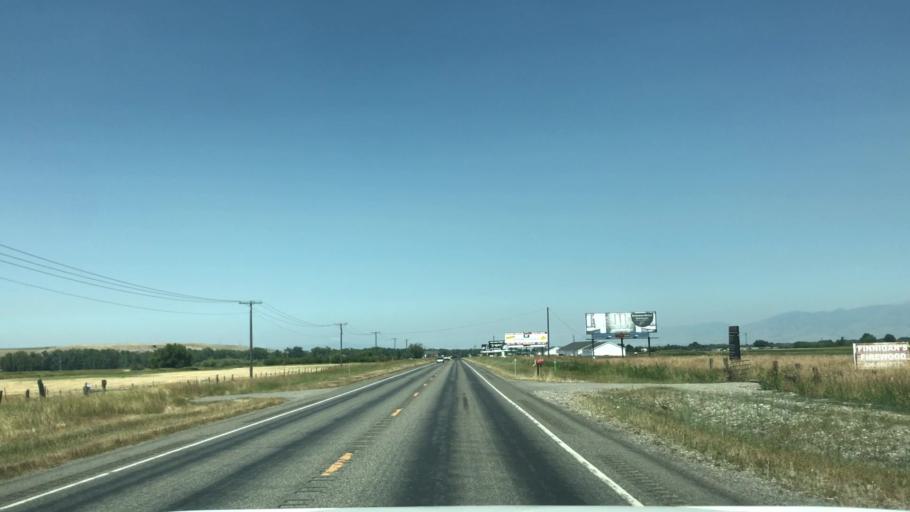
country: US
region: Montana
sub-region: Gallatin County
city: Four Corners
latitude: 45.6310
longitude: -111.1968
